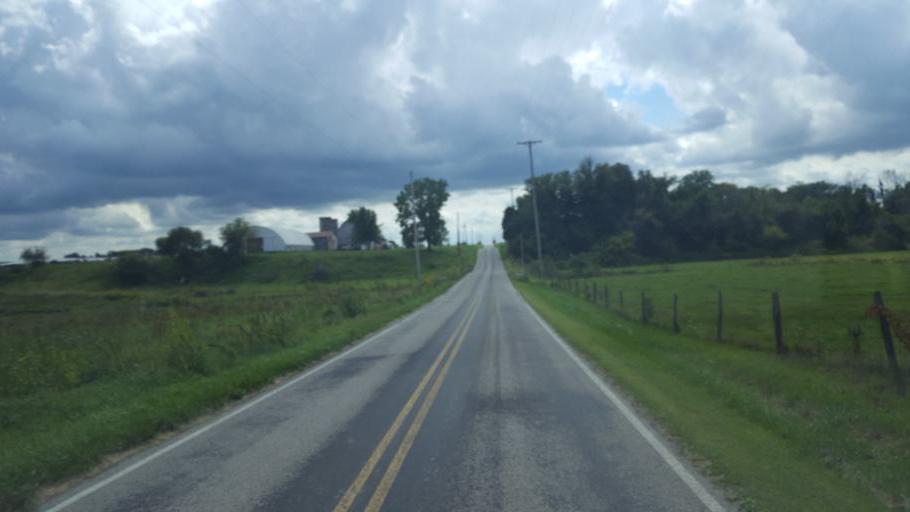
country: US
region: Ohio
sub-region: Huron County
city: Plymouth
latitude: 41.0759
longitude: -82.6424
